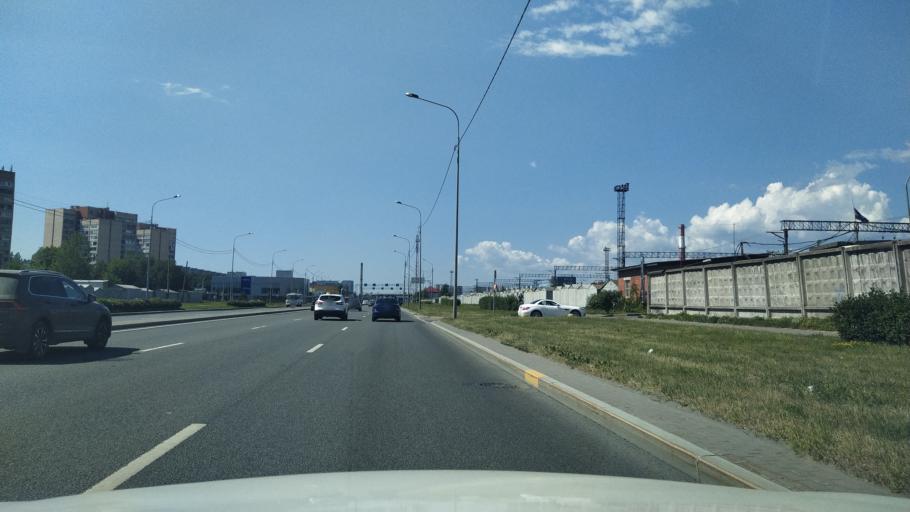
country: RU
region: Leningrad
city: Parnas
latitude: 60.0556
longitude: 30.3658
